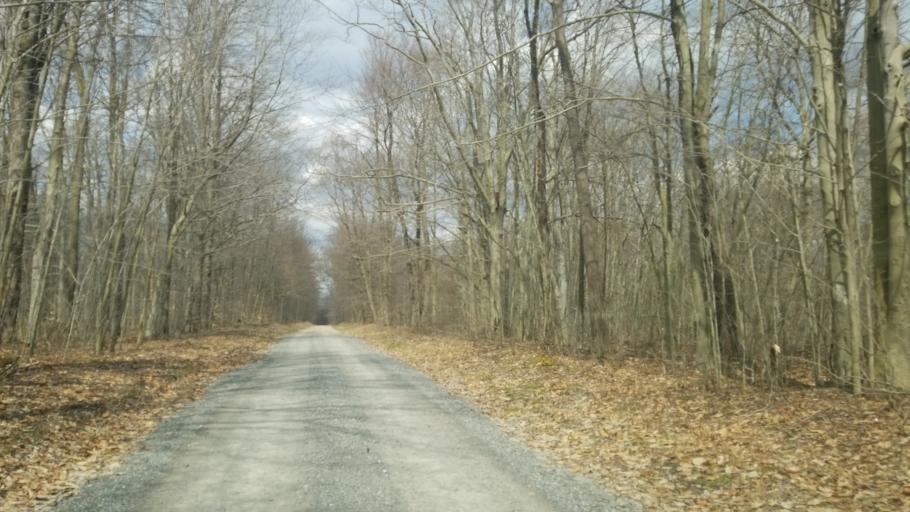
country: US
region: Pennsylvania
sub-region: Clearfield County
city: Clearfield
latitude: 41.1398
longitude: -78.5196
